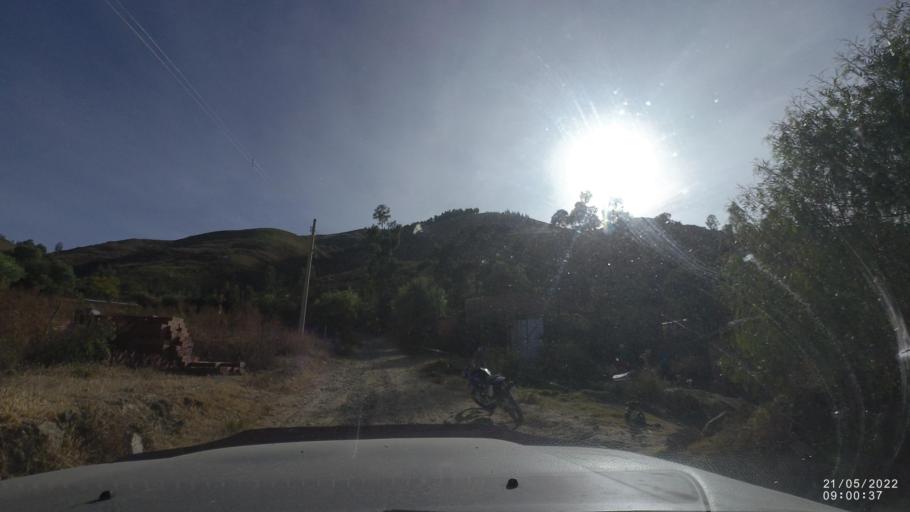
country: BO
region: Cochabamba
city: Cochabamba
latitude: -17.3766
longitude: -66.0349
